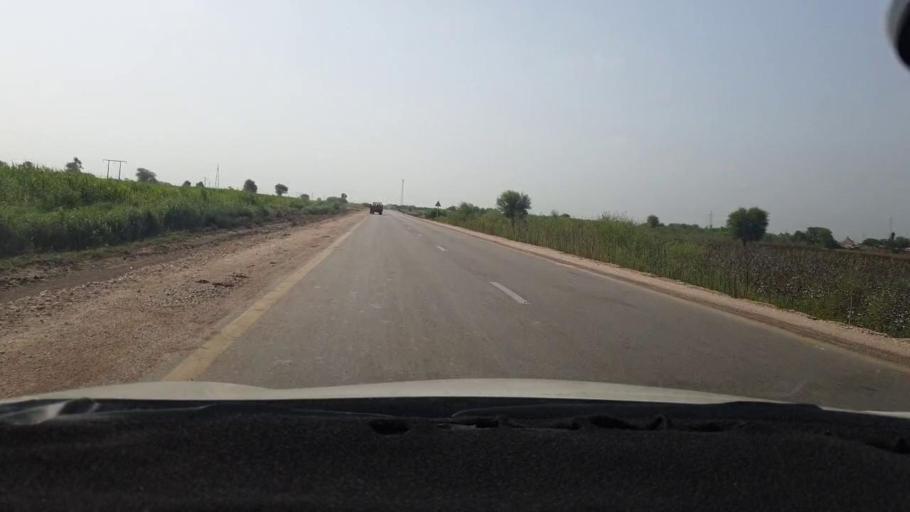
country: PK
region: Sindh
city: Tando Mittha Khan
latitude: 25.8378
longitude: 69.0626
